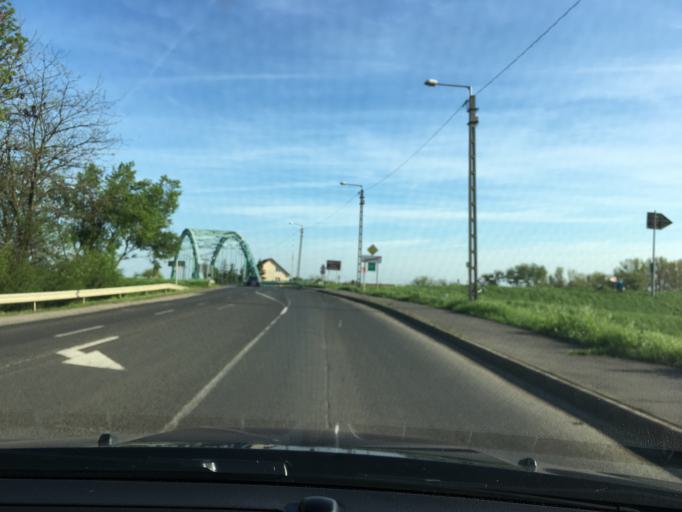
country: HU
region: Bekes
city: Szeghalom
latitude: 47.0145
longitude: 21.1786
